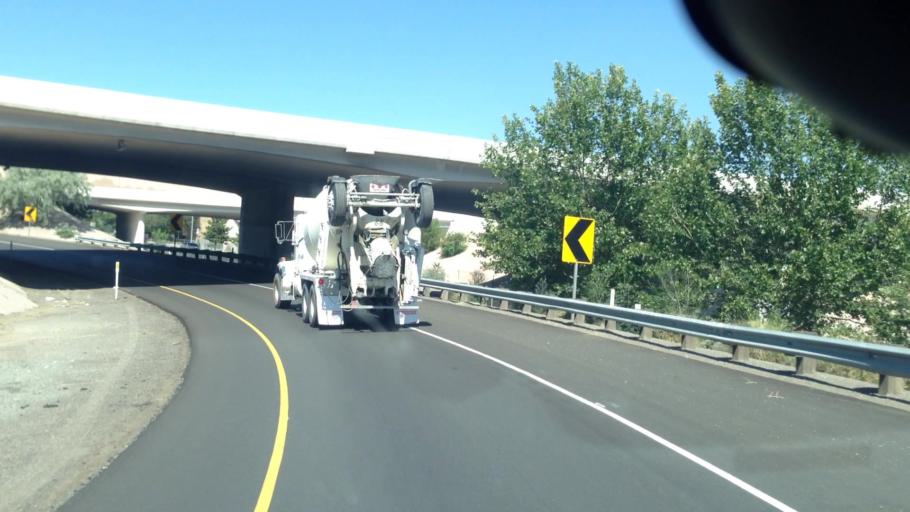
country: US
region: Nevada
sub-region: Washoe County
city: Reno
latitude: 39.5388
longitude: -119.7873
